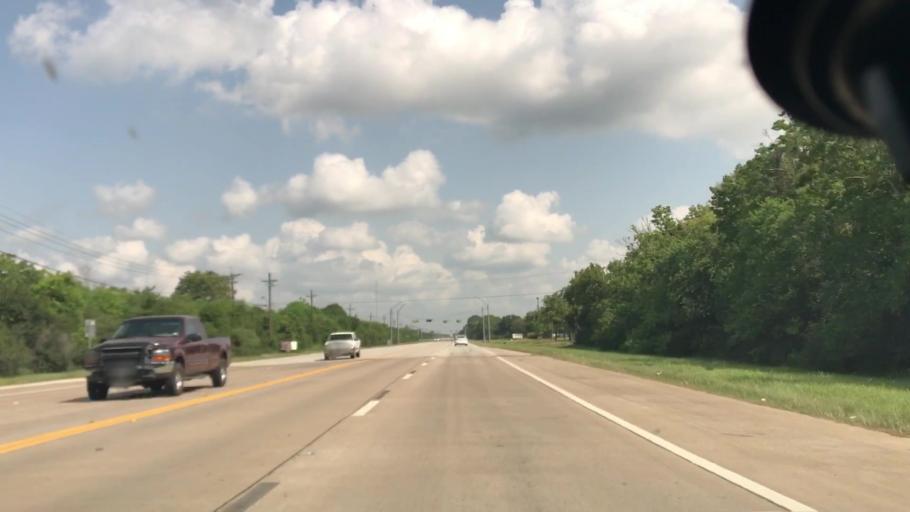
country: US
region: Texas
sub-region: Brazoria County
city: Angleton
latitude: 29.2035
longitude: -95.4351
